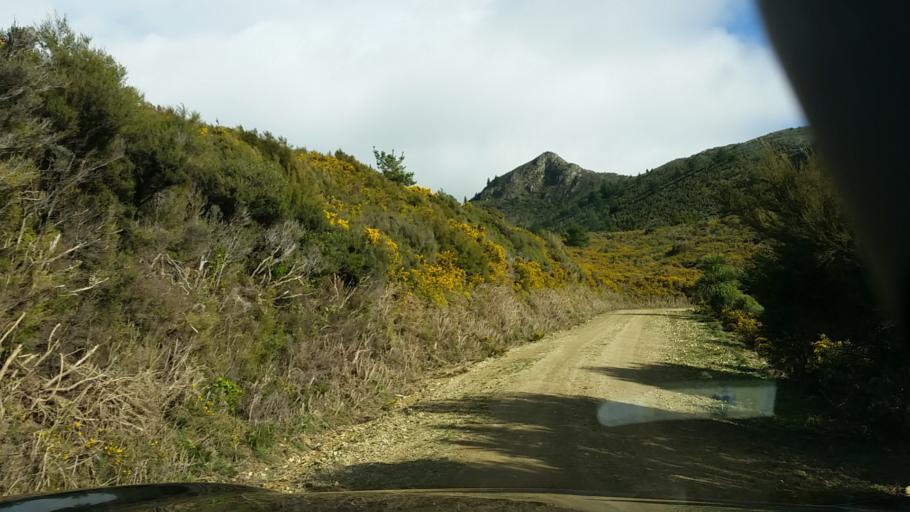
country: NZ
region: Marlborough
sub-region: Marlborough District
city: Picton
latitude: -40.9713
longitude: 173.8945
